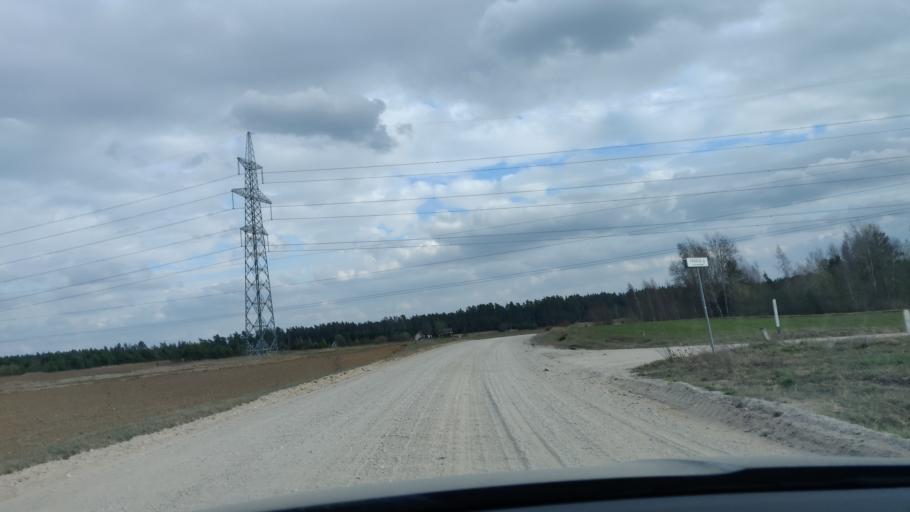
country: LT
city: Lentvaris
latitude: 54.6084
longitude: 25.0732
